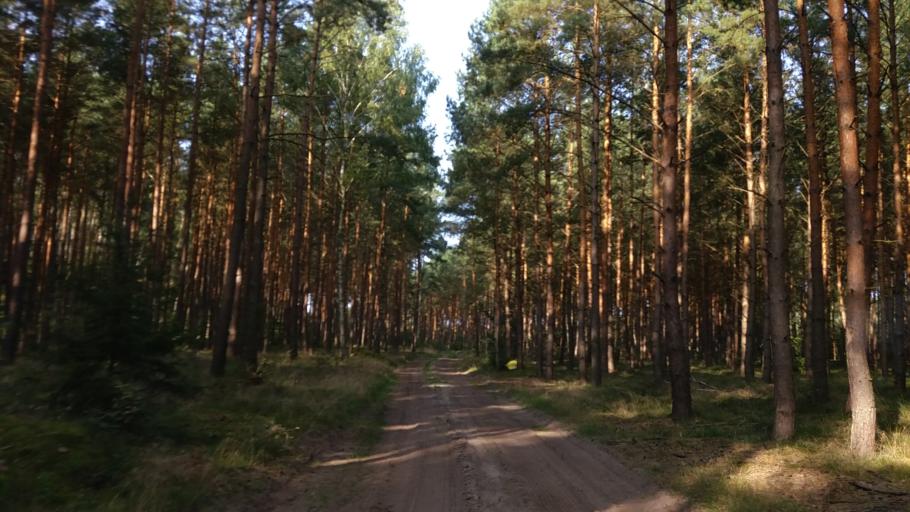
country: PL
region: West Pomeranian Voivodeship
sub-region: Powiat choszczenski
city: Choszczno
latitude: 53.2437
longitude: 15.3992
